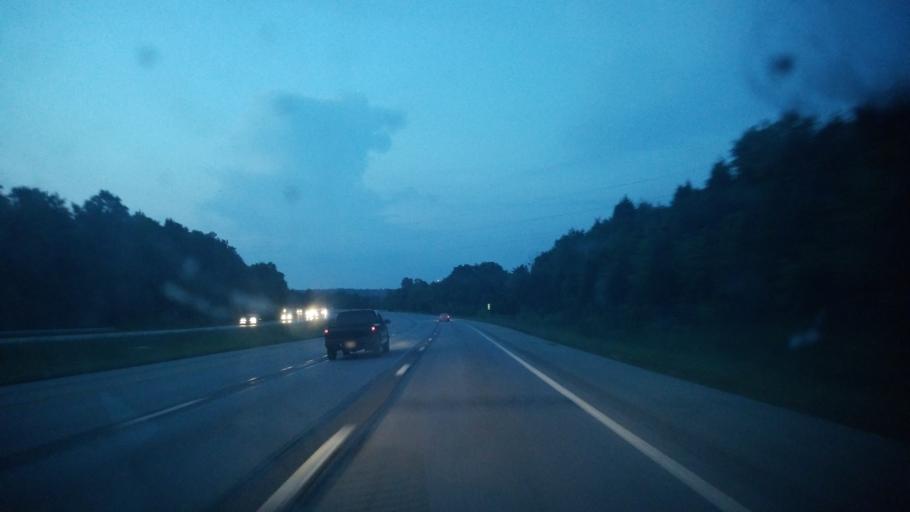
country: US
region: Ohio
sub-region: Clermont County
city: Summerside
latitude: 39.1324
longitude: -84.2672
